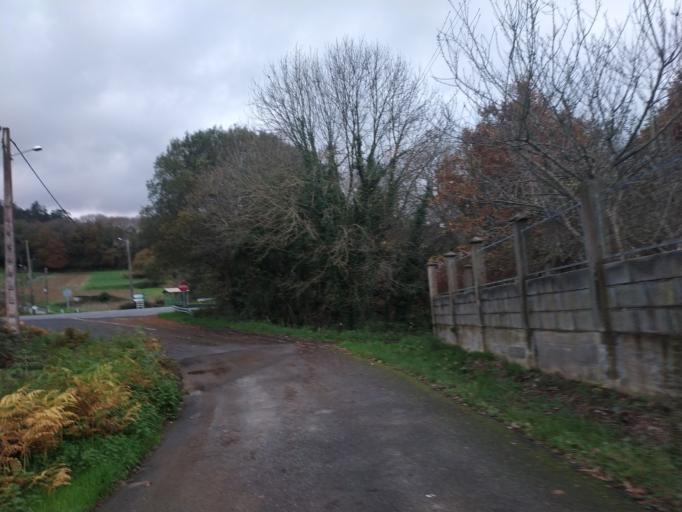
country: ES
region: Galicia
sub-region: Provincia de Pontevedra
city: Silleda
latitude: 42.7813
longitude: -8.1719
